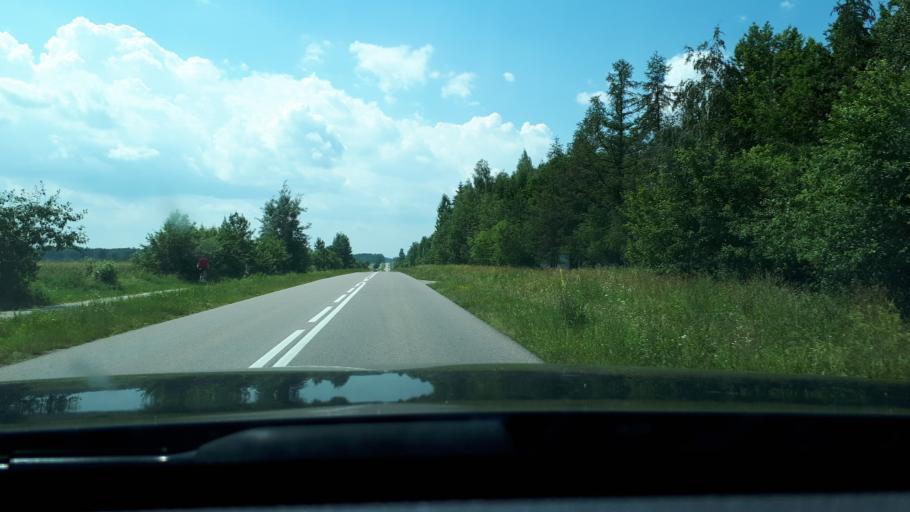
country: PL
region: Podlasie
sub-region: Powiat bialostocki
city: Choroszcz
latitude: 53.1287
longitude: 23.0101
